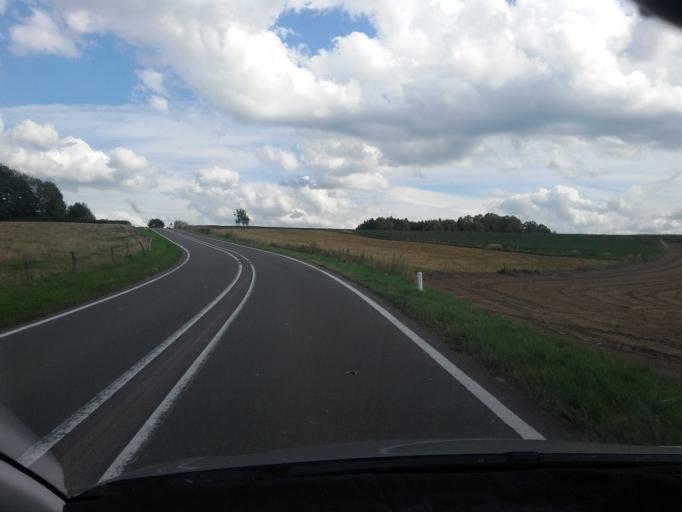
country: BE
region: Wallonia
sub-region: Province du Luxembourg
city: Saint-Hubert
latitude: 50.0305
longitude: 5.3335
